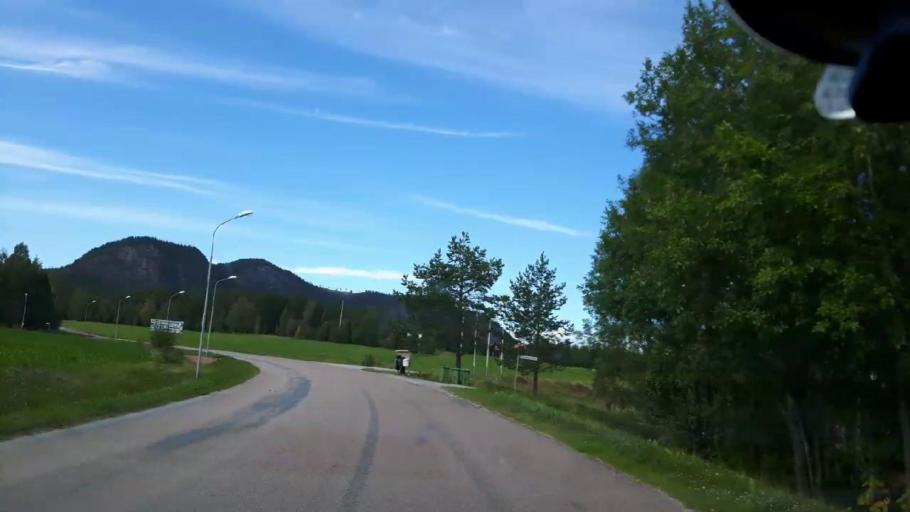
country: SE
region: Jaemtland
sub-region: Ragunda Kommun
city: Hammarstrand
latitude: 63.1152
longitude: 16.3477
